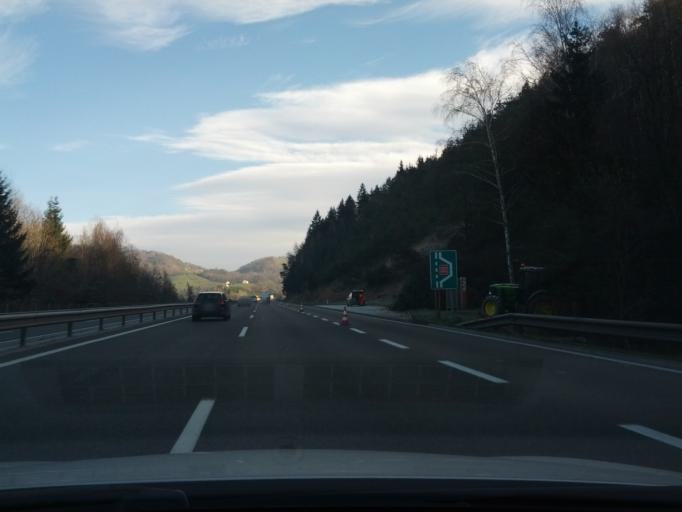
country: SI
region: Slovenska Konjice
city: Slovenske Konjice
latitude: 46.2801
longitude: 15.4227
